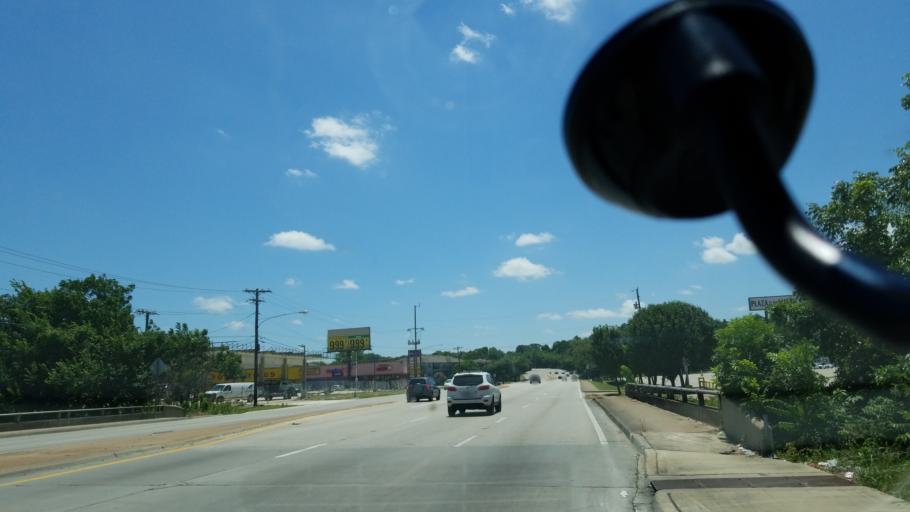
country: US
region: Texas
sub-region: Dallas County
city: Cockrell Hill
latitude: 32.6863
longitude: -96.8211
